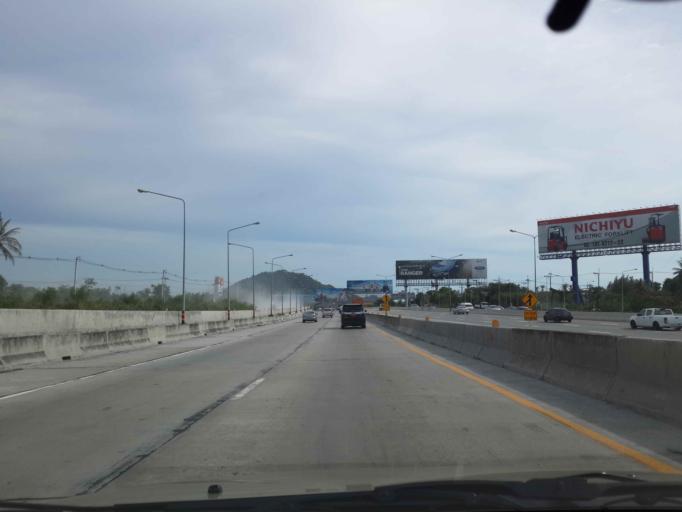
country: TH
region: Chon Buri
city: Chon Buri
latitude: 13.2976
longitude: 100.9947
